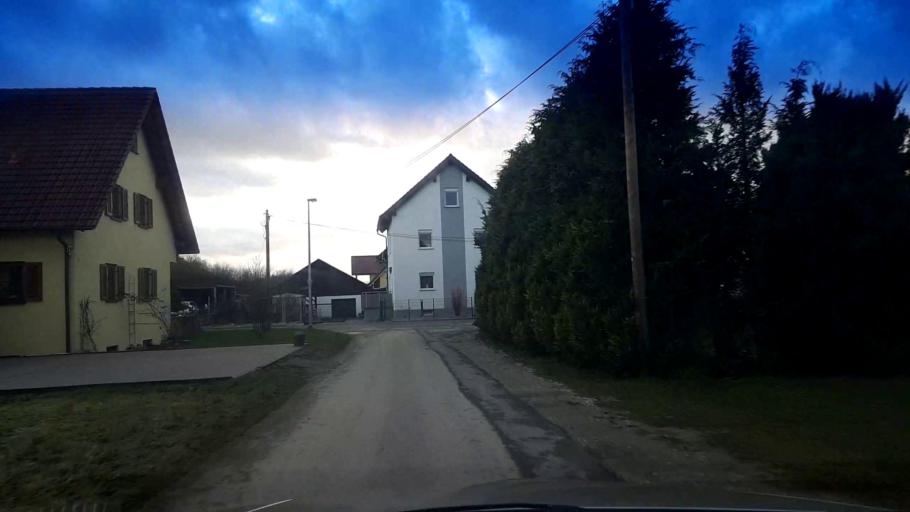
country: DE
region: Bavaria
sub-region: Upper Franconia
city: Buttenheim
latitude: 49.8064
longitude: 11.0565
